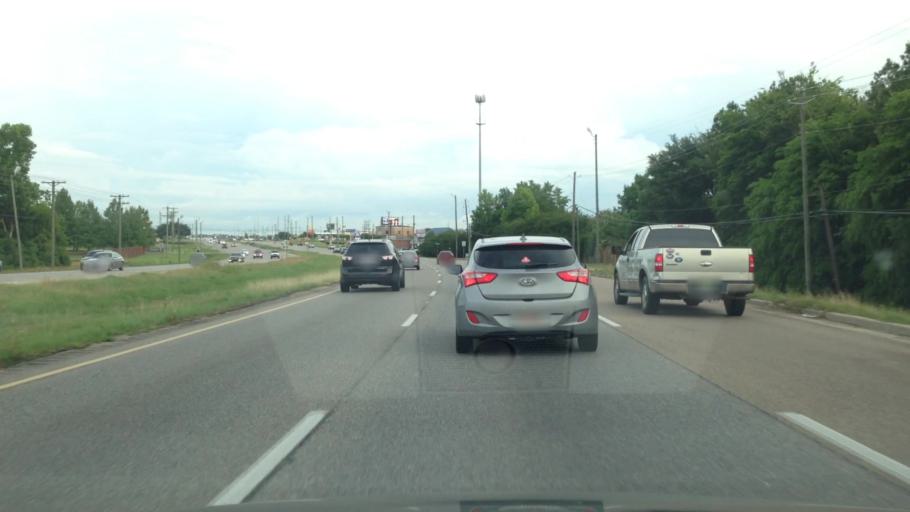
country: US
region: Alabama
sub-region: Montgomery County
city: Pike Road
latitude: 32.3448
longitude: -86.1791
